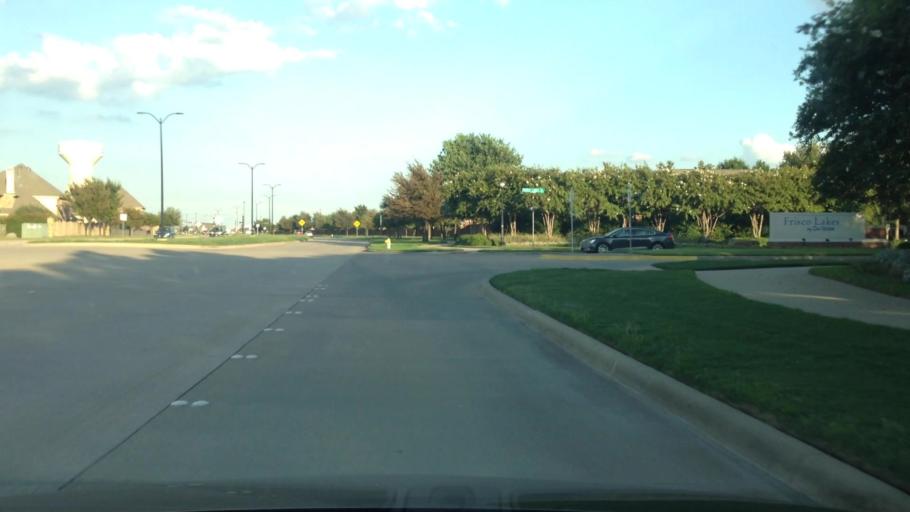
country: US
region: Texas
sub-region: Denton County
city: Little Elm
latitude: 33.1452
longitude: -96.8968
